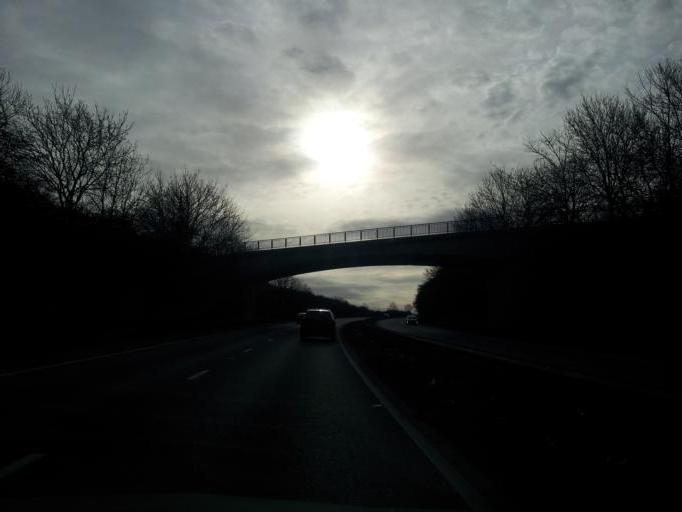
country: GB
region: England
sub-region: Lincolnshire
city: Stamford
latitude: 52.6367
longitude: -0.4808
